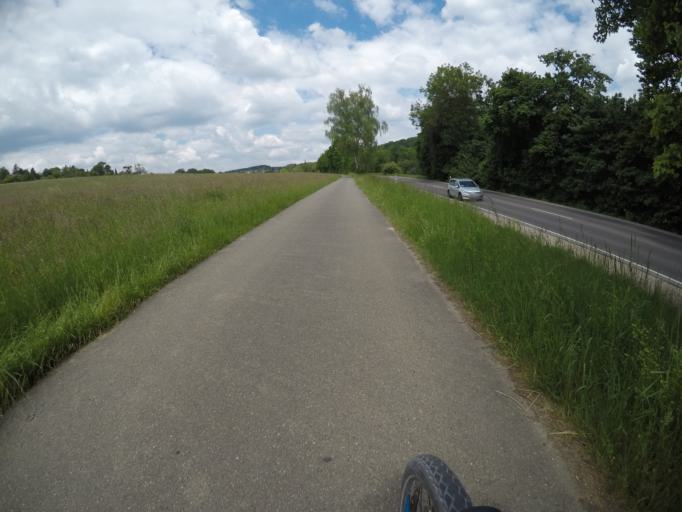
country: DE
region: Baden-Wuerttemberg
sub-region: Regierungsbezirk Stuttgart
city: Ostfildern
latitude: 48.7216
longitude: 9.2172
